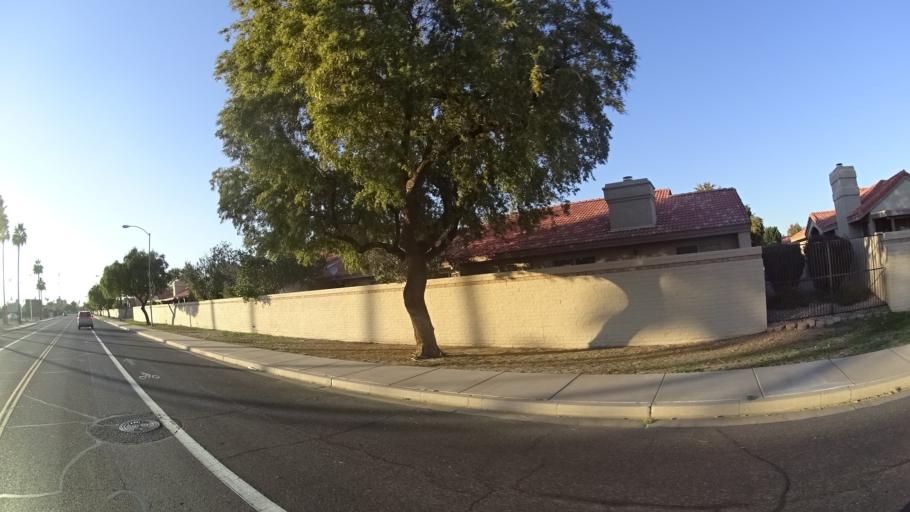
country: US
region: Arizona
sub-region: Maricopa County
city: Mesa
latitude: 33.4296
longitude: -111.8259
